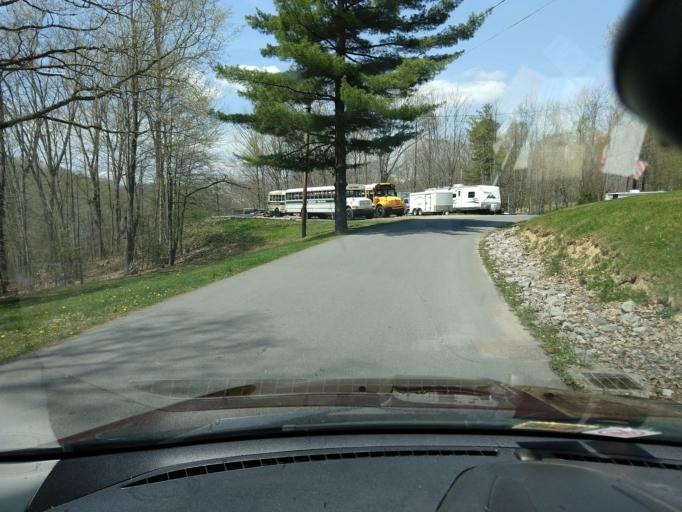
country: US
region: West Virginia
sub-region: Raleigh County
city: Bradley
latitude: 37.8542
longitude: -81.2050
